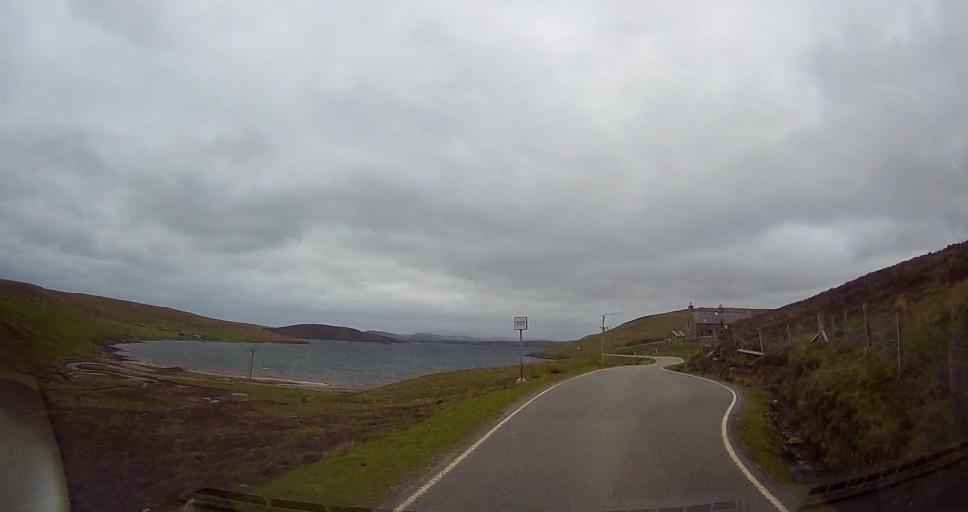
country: GB
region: Scotland
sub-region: Shetland Islands
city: Lerwick
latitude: 60.3322
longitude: -1.3354
